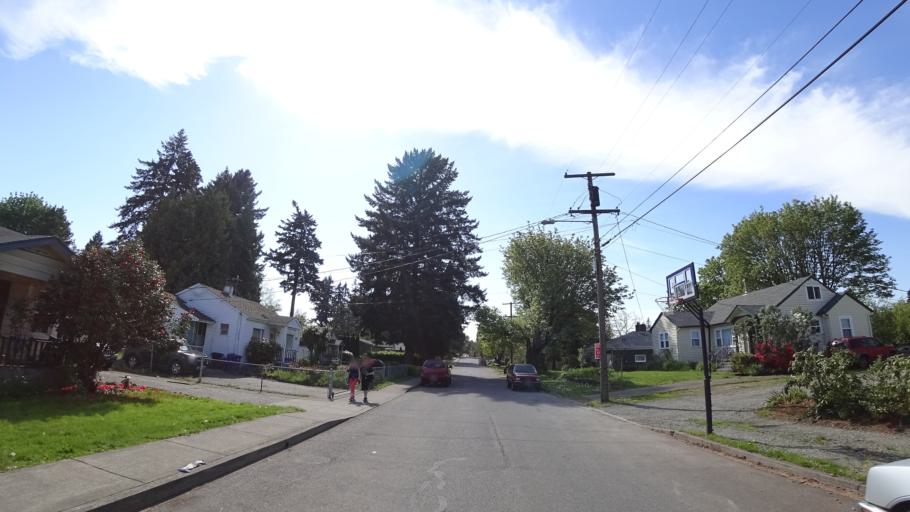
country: US
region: Oregon
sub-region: Clackamas County
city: Milwaukie
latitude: 45.4549
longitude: -122.6230
